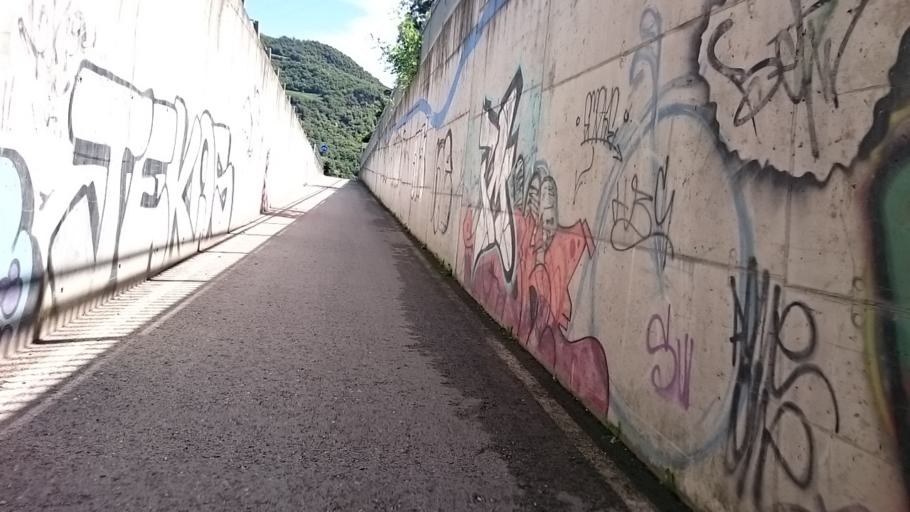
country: IT
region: Trentino-Alto Adige
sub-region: Bolzano
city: Cornedo All'Isarco
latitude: 46.4930
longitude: 11.4032
